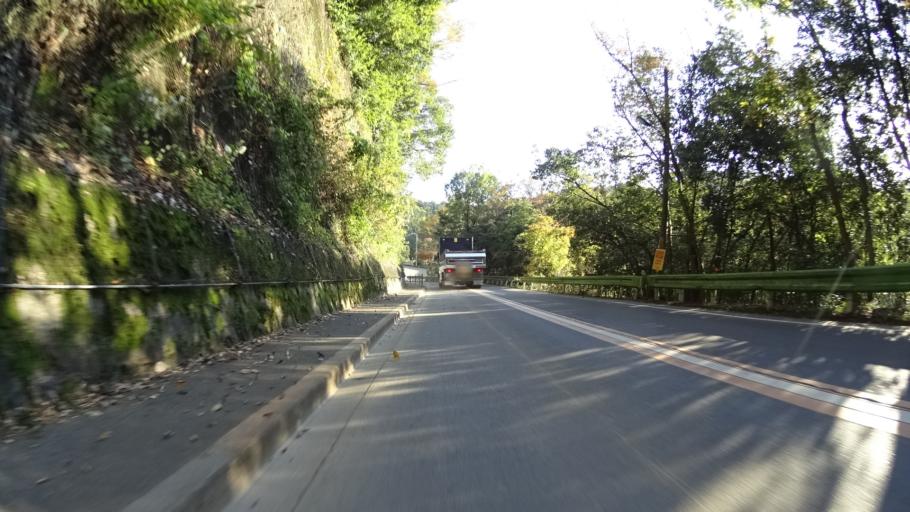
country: JP
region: Tokyo
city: Itsukaichi
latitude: 35.6677
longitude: 139.2461
